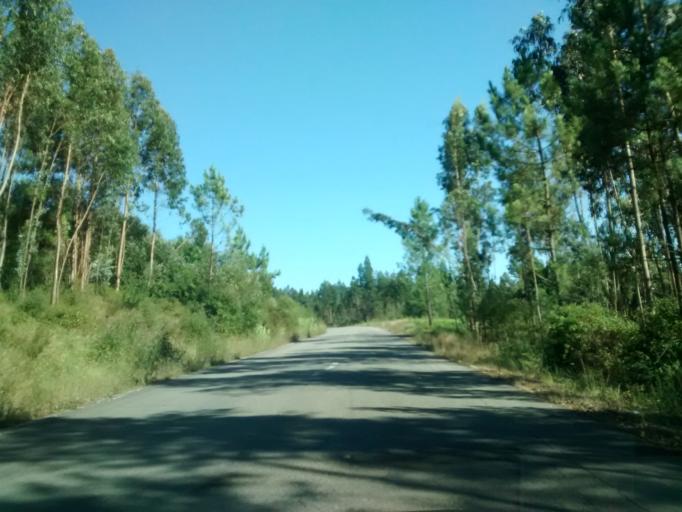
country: PT
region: Coimbra
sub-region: Cantanhede
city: Cantanhede
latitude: 40.4256
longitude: -8.6221
